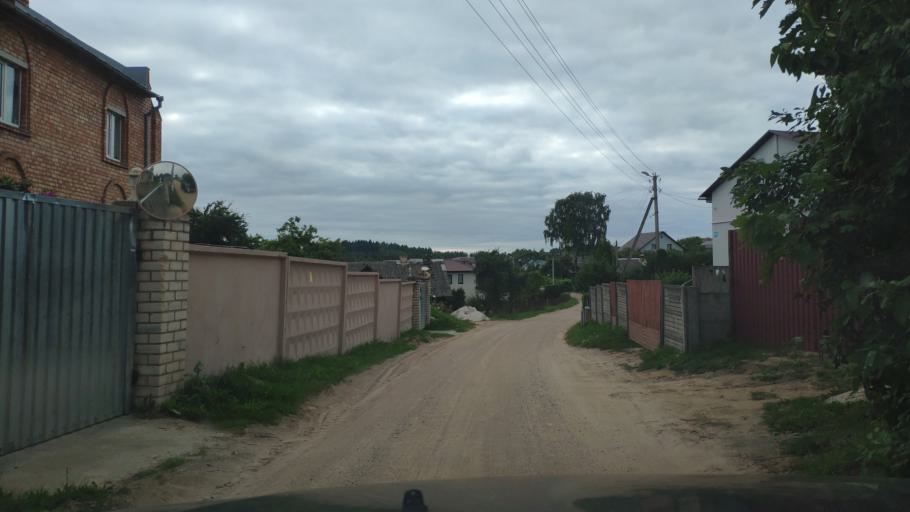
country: BY
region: Minsk
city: Novosel'ye
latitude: 53.9262
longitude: 27.2543
